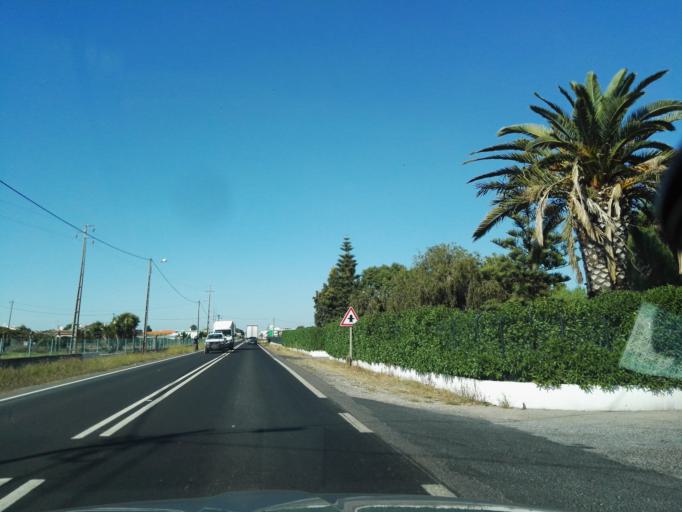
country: PT
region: Santarem
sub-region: Benavente
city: Samora Correia
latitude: 38.9130
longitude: -8.8815
